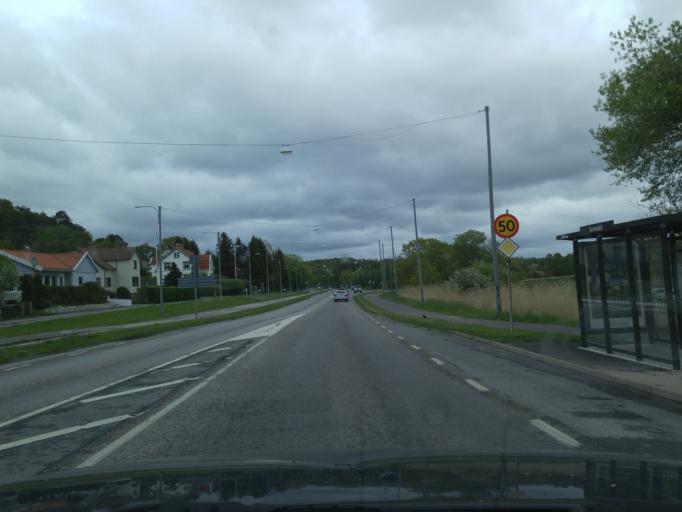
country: SE
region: Vaestra Goetaland
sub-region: Goteborg
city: Majorna
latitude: 57.6370
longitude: 11.9091
